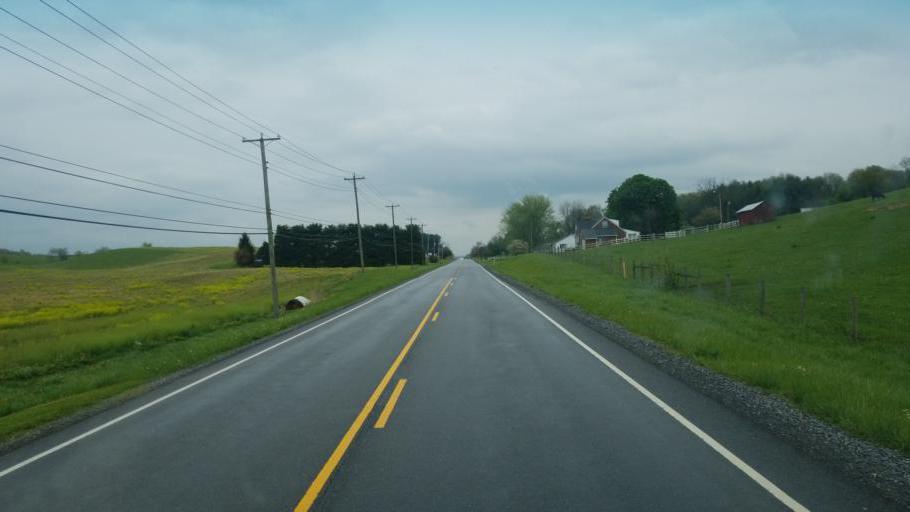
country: US
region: Virginia
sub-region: Smyth County
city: Atkins
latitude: 36.8879
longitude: -81.3654
